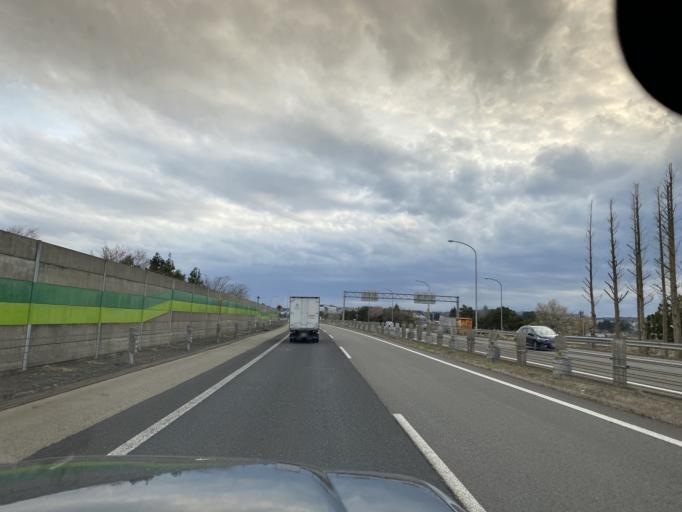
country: JP
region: Niigata
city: Nagaoka
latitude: 37.4585
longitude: 138.7912
